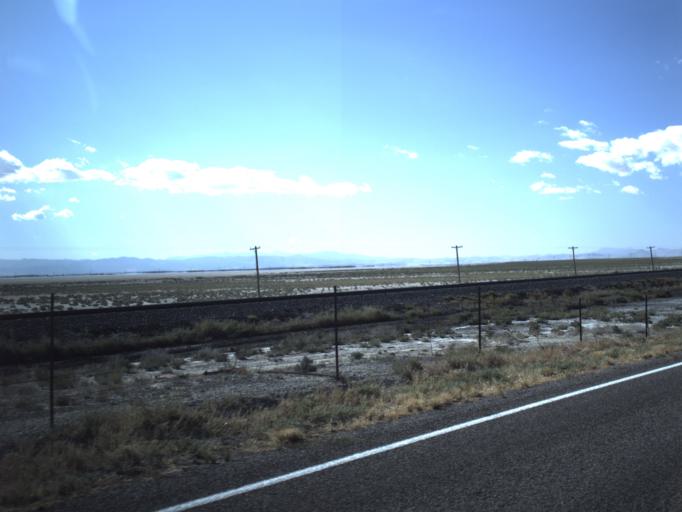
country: US
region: Utah
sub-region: Millard County
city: Delta
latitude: 39.1783
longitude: -112.7017
